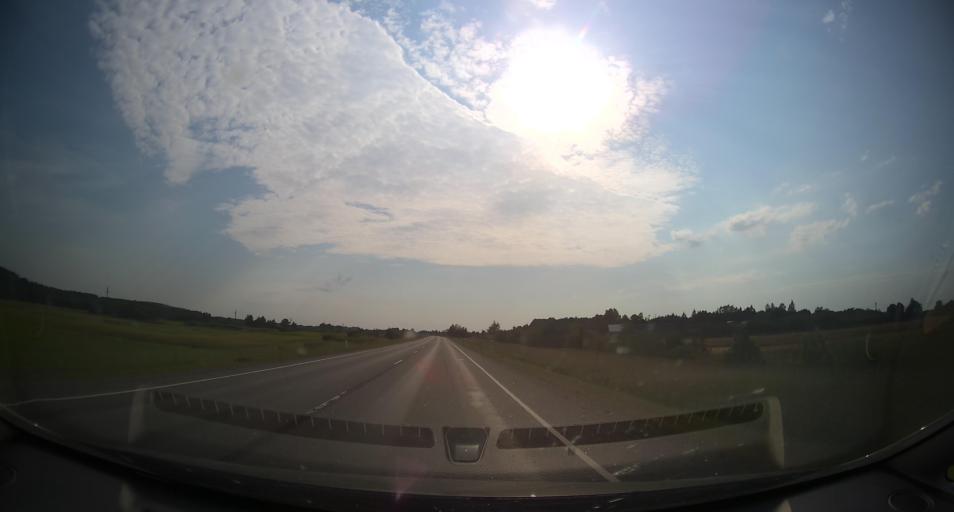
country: EE
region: Laeaene
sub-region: Lihula vald
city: Lihula
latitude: 58.7114
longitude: 23.8866
